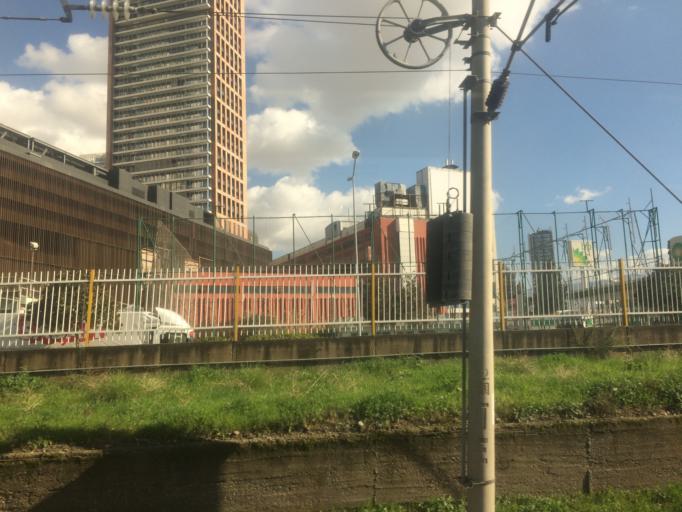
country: TR
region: Izmir
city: Izmir
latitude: 38.4467
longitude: 27.1732
